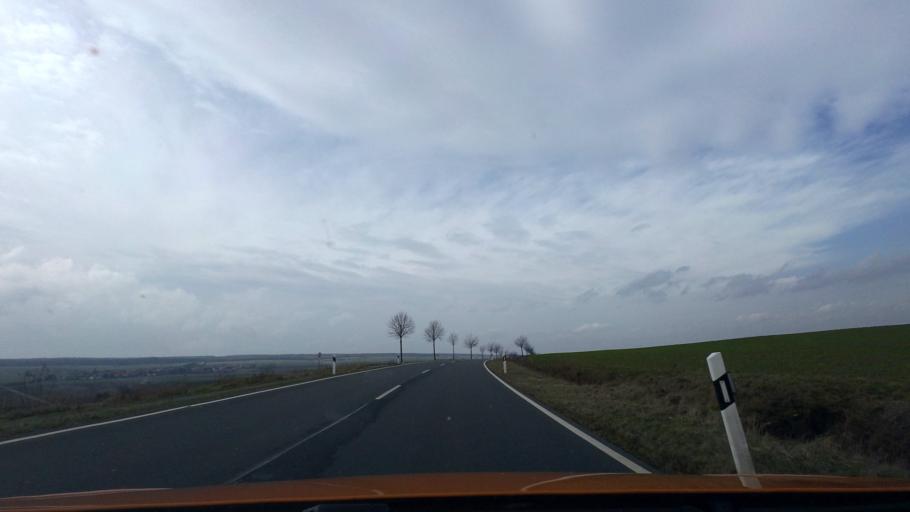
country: DE
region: Lower Saxony
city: Supplingen
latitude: 52.2268
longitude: 10.8814
